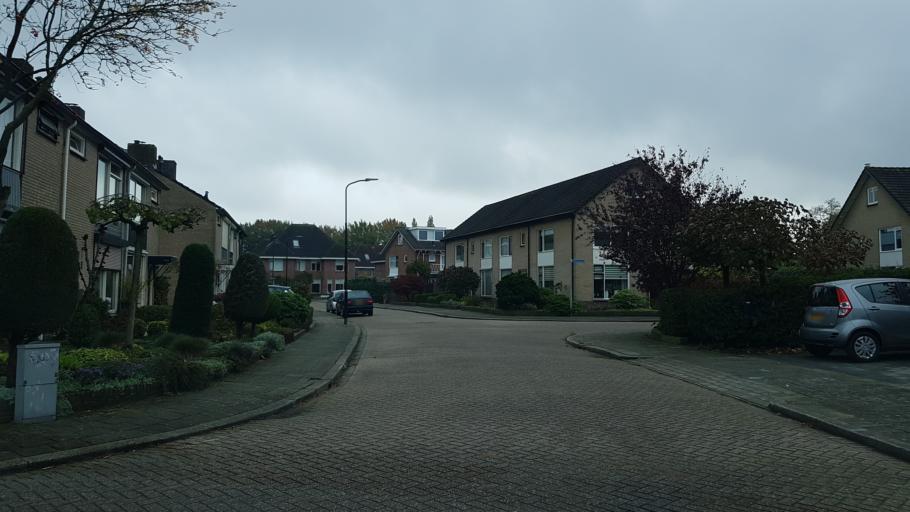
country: NL
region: Gelderland
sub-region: Gemeente Apeldoorn
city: Apeldoorn
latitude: 52.2179
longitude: 5.9437
